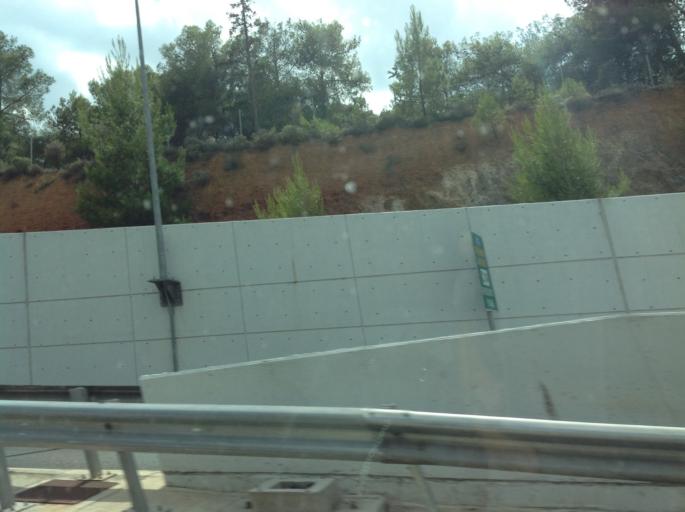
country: GR
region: Attica
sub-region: Nomarchia Athinas
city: Agia Paraskevi
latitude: 38.0067
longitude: 23.8367
